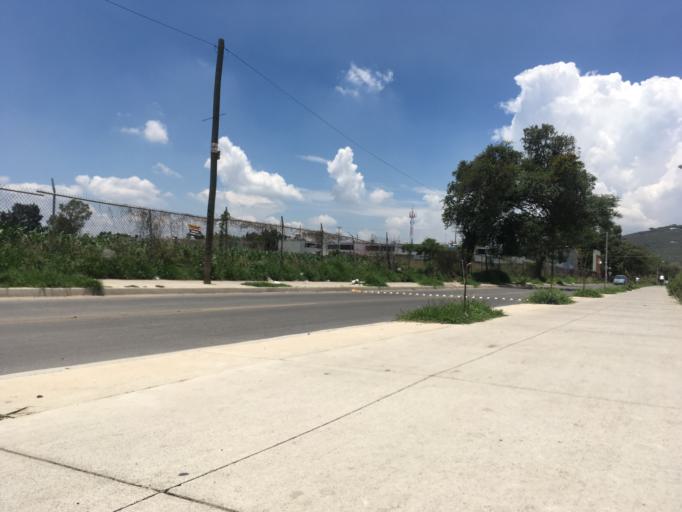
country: MX
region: Jalisco
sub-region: Tlajomulco de Zuniga
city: Jardines de San Sebastian
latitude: 20.5209
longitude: -103.4249
